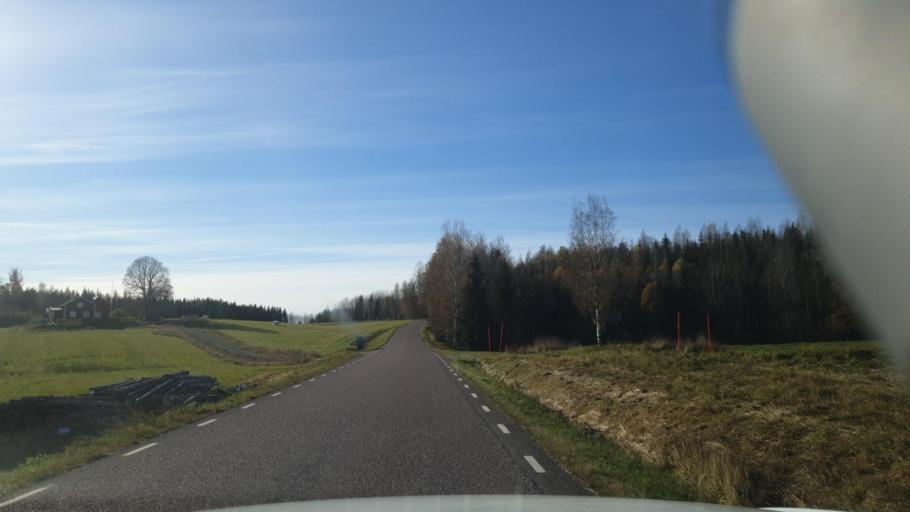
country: SE
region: Vaermland
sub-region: Karlstads Kommun
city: Edsvalla
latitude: 59.4879
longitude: 13.0929
